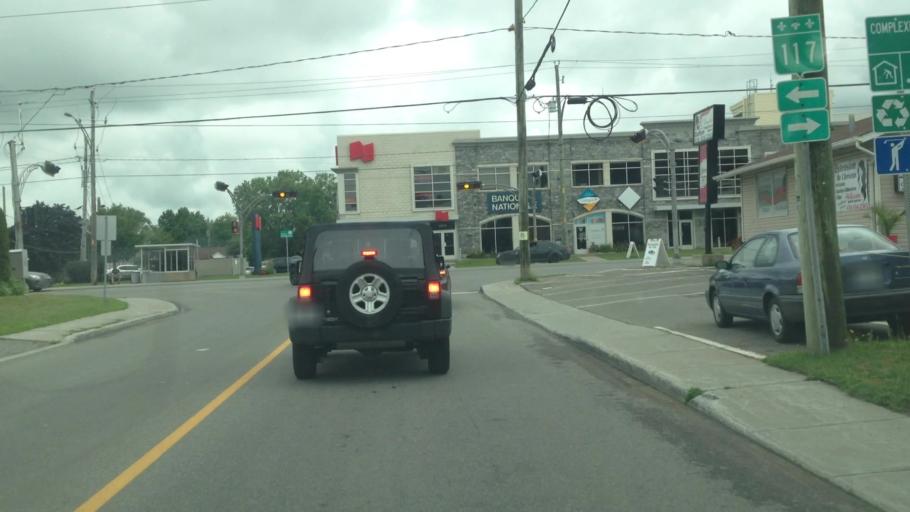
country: CA
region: Quebec
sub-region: Laurentides
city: Blainville
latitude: 45.7027
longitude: -73.9264
